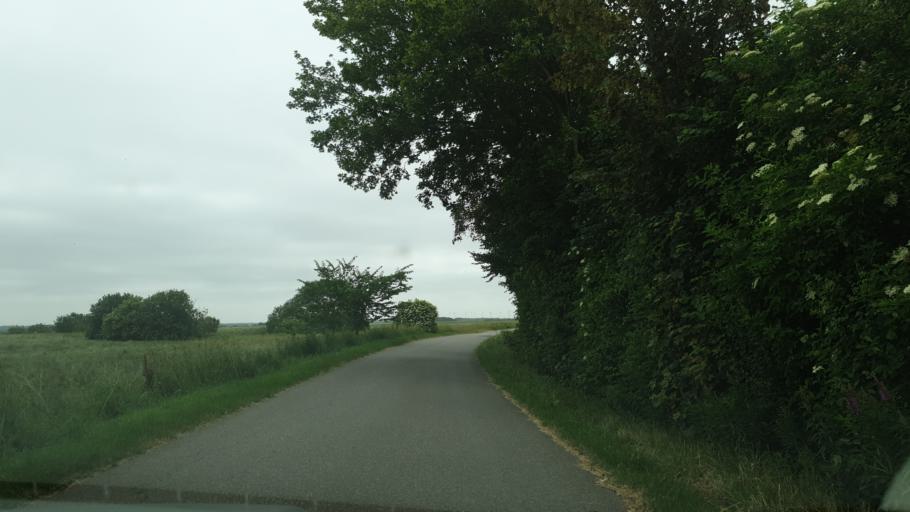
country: DK
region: Central Jutland
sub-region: Ringkobing-Skjern Kommune
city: Skjern
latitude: 55.9343
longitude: 8.4022
